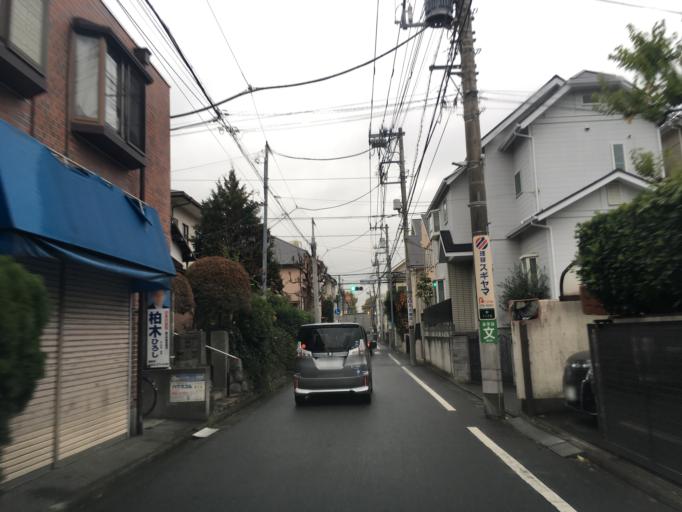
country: JP
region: Tokyo
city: Kokubunji
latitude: 35.6971
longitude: 139.4411
